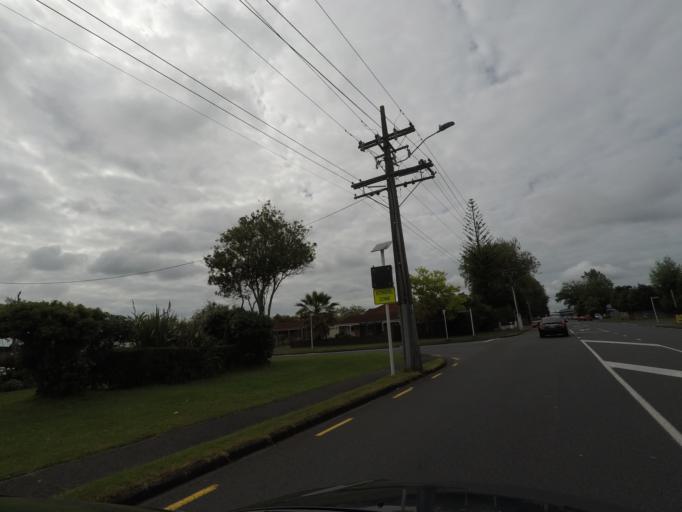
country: NZ
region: Auckland
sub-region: Auckland
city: Rosebank
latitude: -36.8650
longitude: 174.6153
